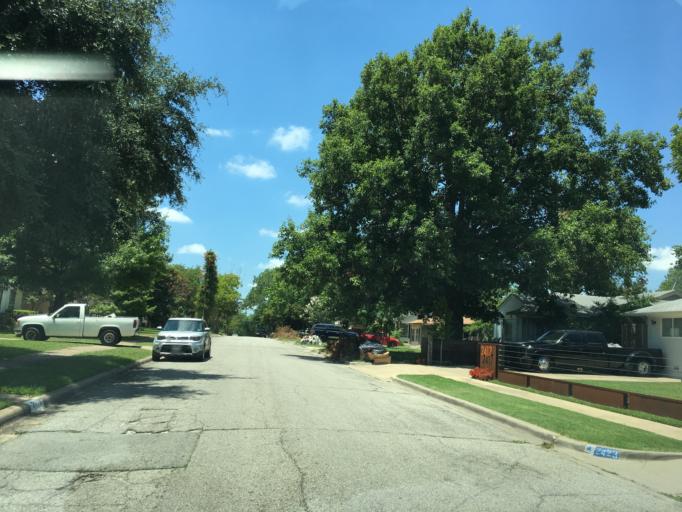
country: US
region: Texas
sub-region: Dallas County
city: Garland
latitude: 32.8497
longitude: -96.6708
